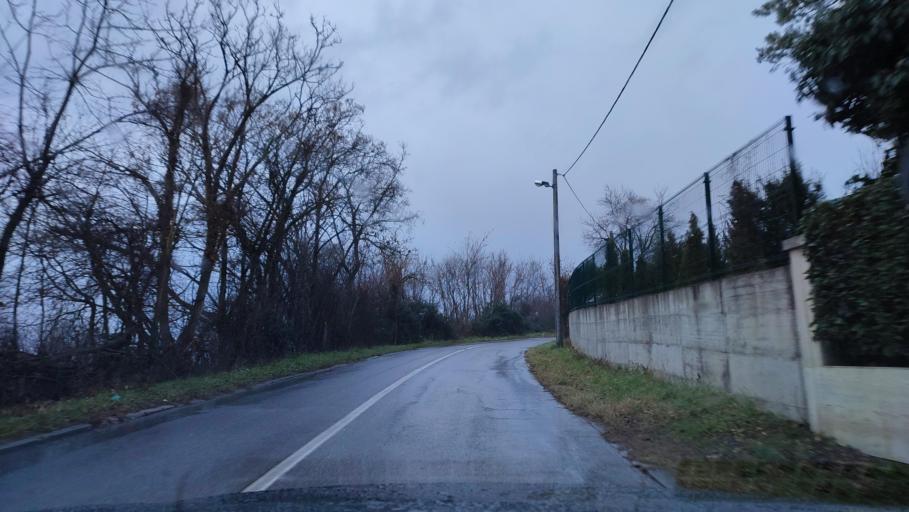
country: HR
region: Grad Zagreb
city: Zagreb
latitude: 45.8432
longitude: 15.9640
